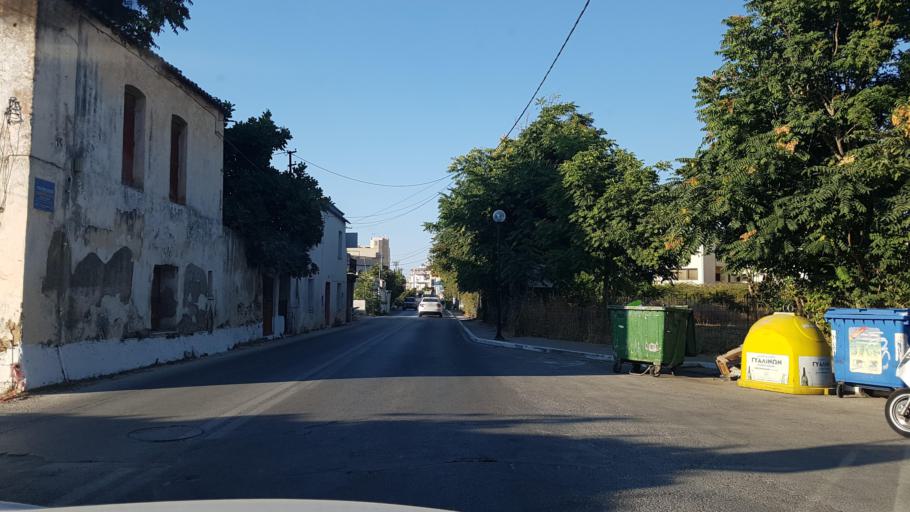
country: GR
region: Crete
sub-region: Nomos Chanias
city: Chania
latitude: 35.5056
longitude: 24.0081
